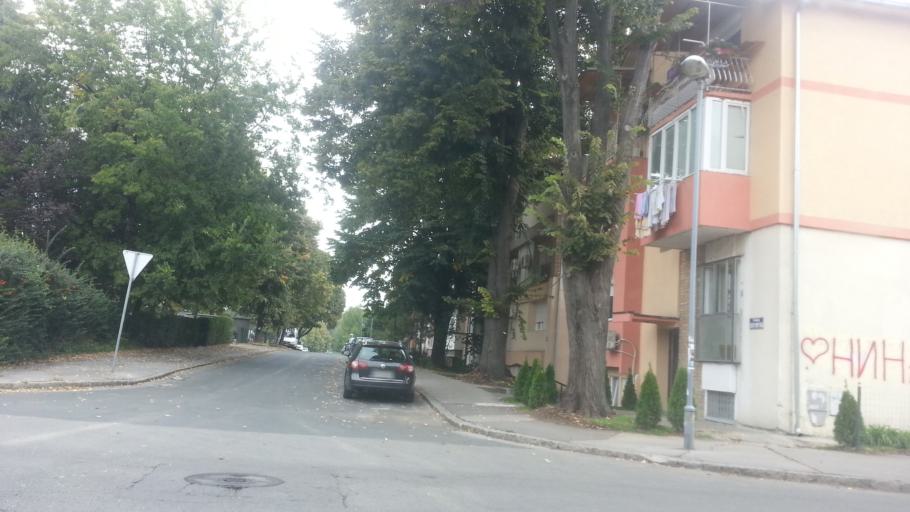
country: RS
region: Central Serbia
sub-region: Belgrade
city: Zemun
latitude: 44.8588
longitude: 20.3667
